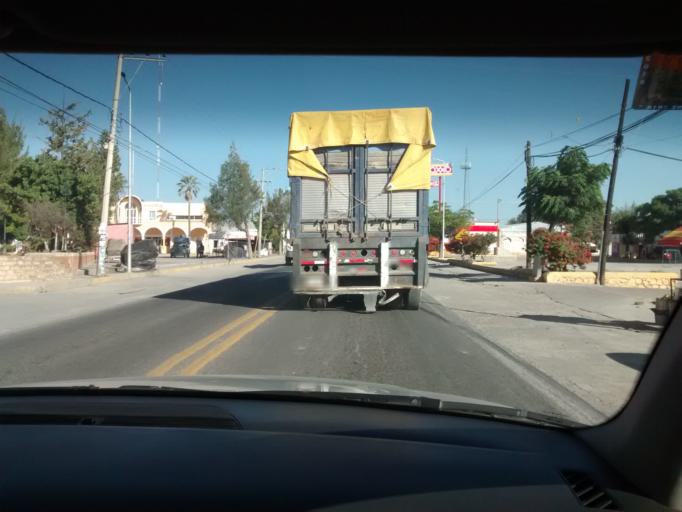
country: MX
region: Puebla
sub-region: Tepanco de Lopez
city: San Andres Cacaloapan
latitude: 18.5548
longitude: -97.5604
